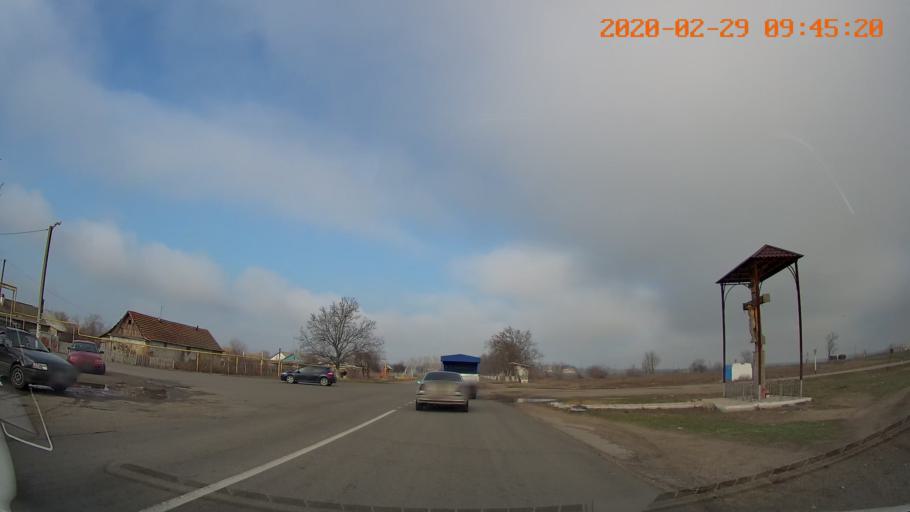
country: MD
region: Telenesti
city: Crasnoe
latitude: 46.6591
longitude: 29.8107
